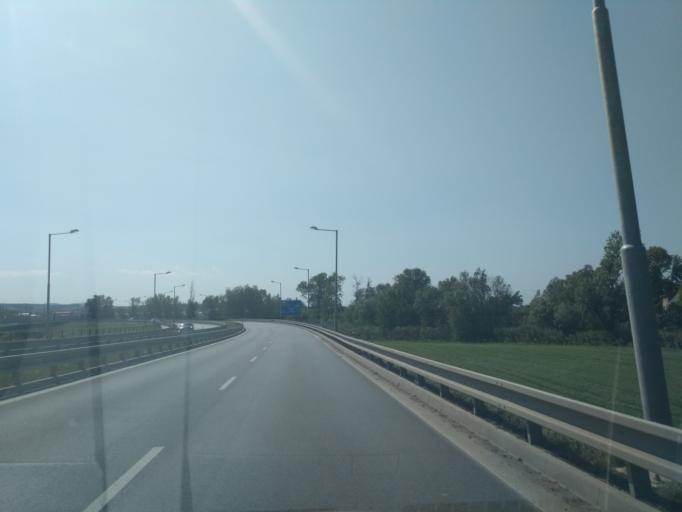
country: SK
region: Presovsky
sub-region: Okres Presov
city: Presov
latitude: 48.9714
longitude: 21.2464
